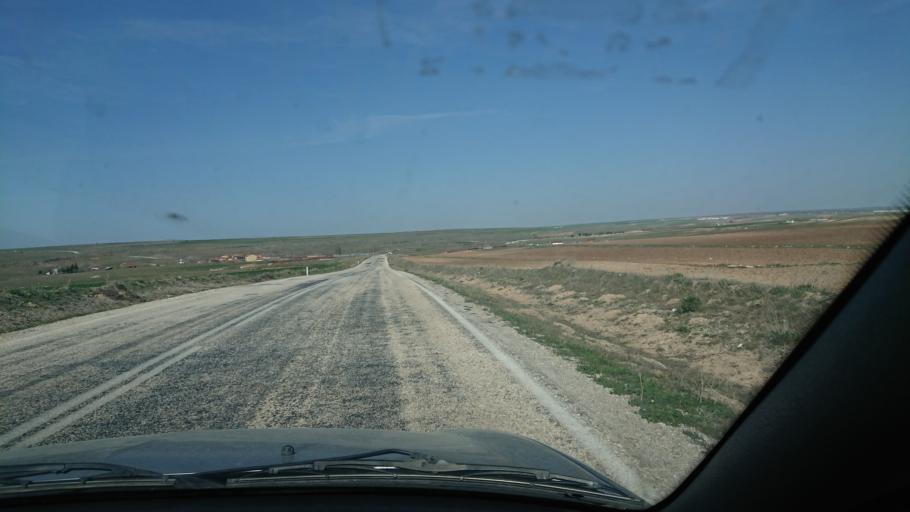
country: TR
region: Eskisehir
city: Eskisehir
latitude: 39.6710
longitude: 30.4757
